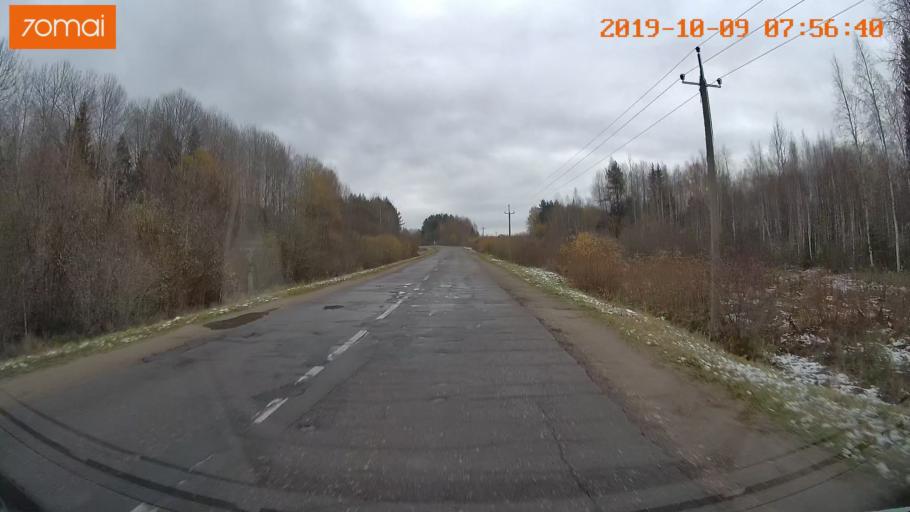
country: RU
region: Jaroslavl
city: Kukoboy
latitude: 58.6975
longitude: 39.9386
